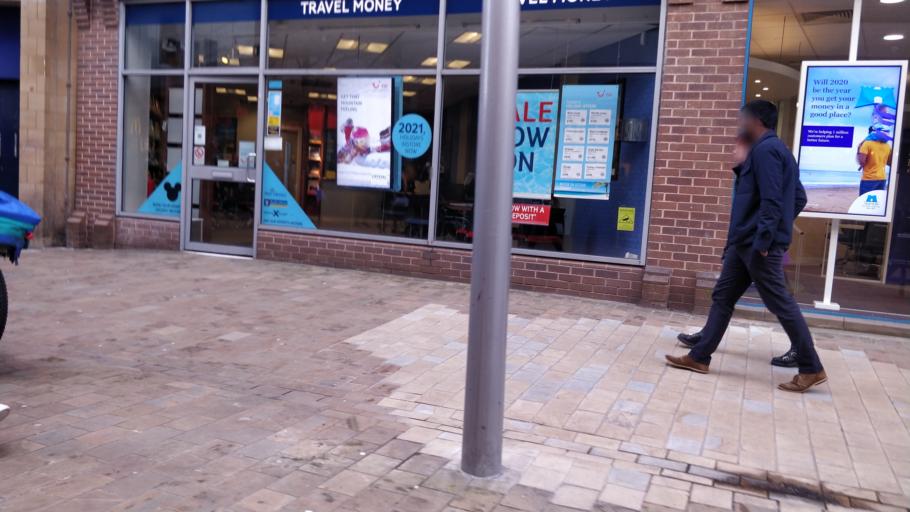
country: GB
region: England
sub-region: City and Borough of Leeds
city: Leeds
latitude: 53.7975
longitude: -1.5463
